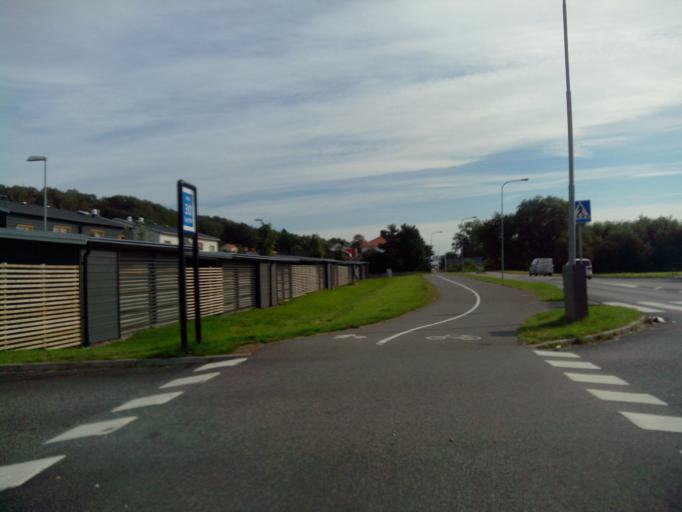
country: SE
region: Vaestra Goetaland
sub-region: Goteborg
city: Goeteborg
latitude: 57.7346
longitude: 11.9578
